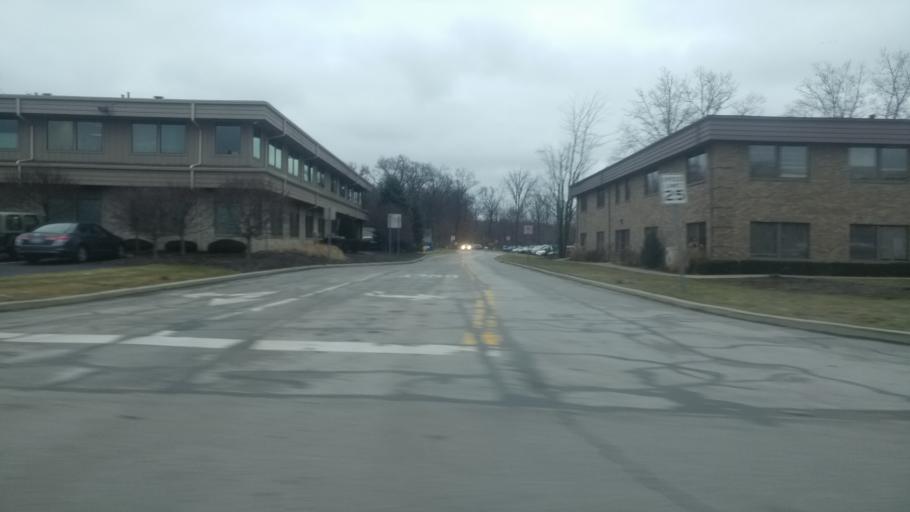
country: US
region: Ohio
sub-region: Lucas County
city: Sylvania
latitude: 41.6753
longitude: -83.7006
